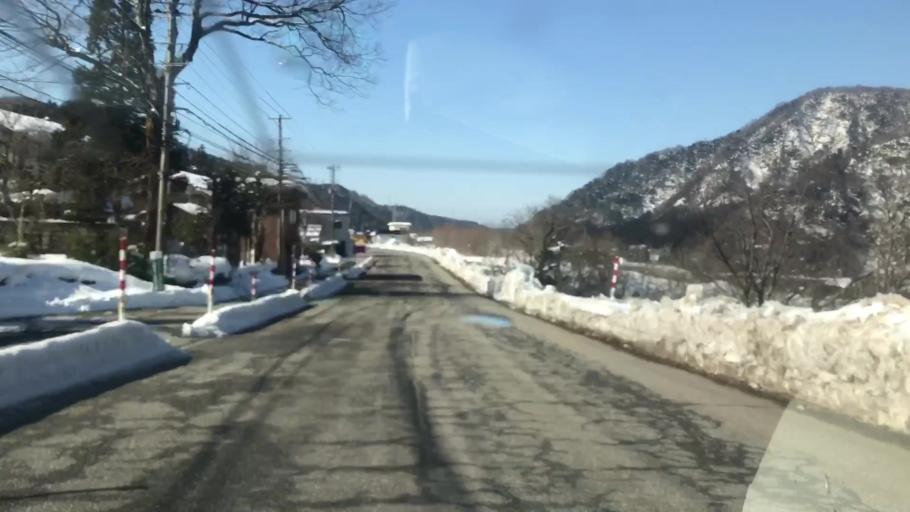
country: JP
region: Toyama
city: Kamiichi
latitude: 36.5695
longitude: 137.3607
